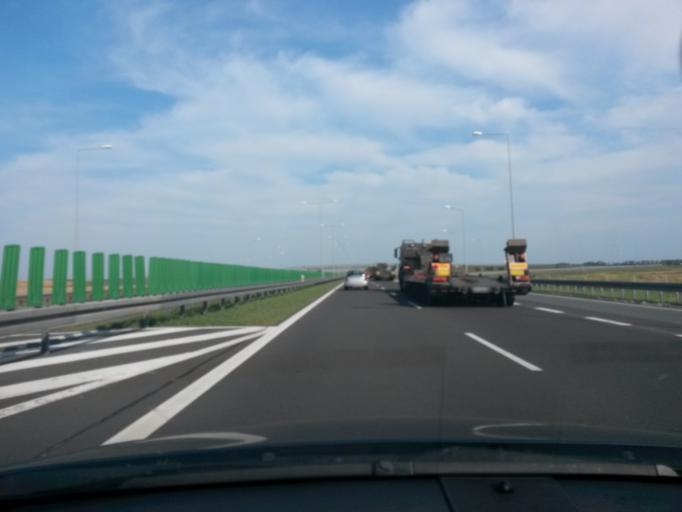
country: PL
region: Greater Poland Voivodeship
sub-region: Powiat slupecki
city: Strzalkowo
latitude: 52.2553
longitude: 17.8134
